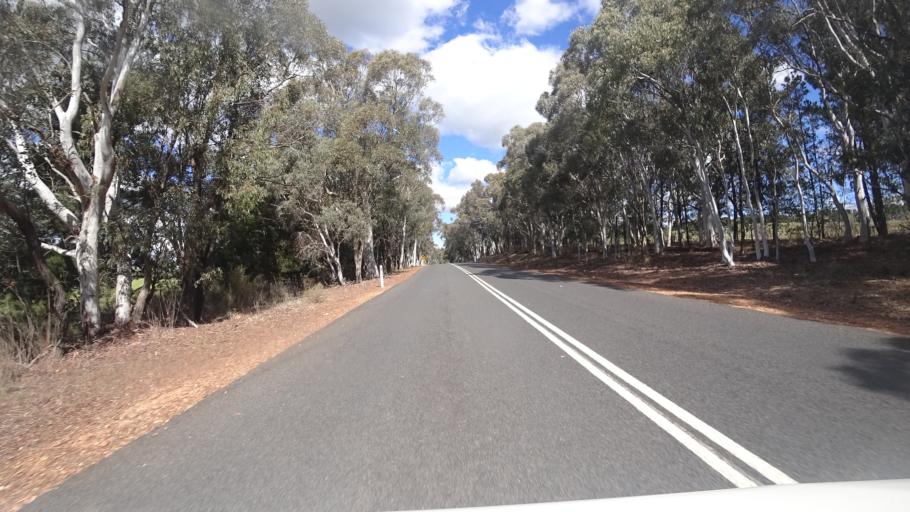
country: AU
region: New South Wales
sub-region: Oberon
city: Oberon
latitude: -33.6709
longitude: 149.7830
